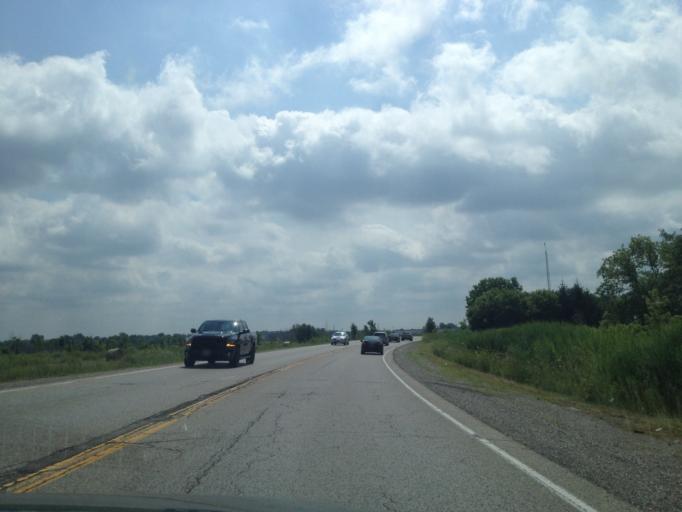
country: CA
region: Ontario
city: London
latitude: 43.0262
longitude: -81.1641
